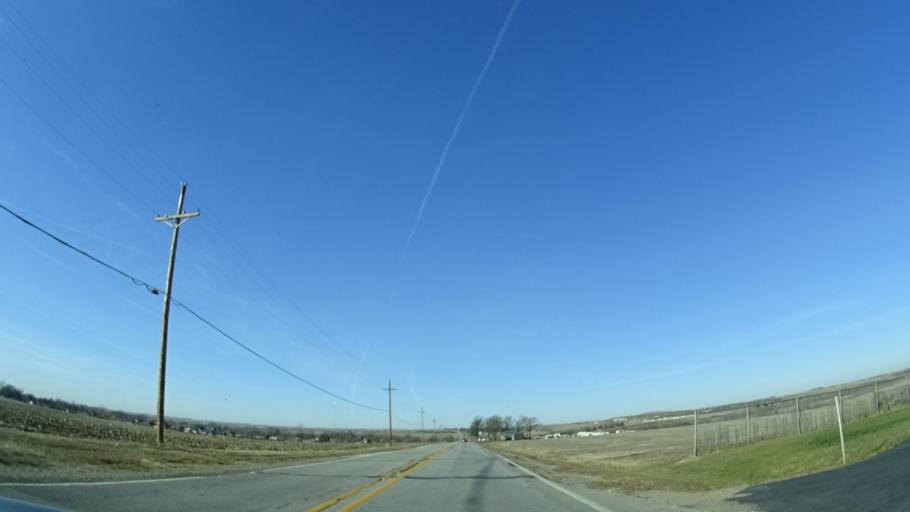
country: US
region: Nebraska
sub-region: Sarpy County
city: Springfield
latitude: 41.0891
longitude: -96.1213
